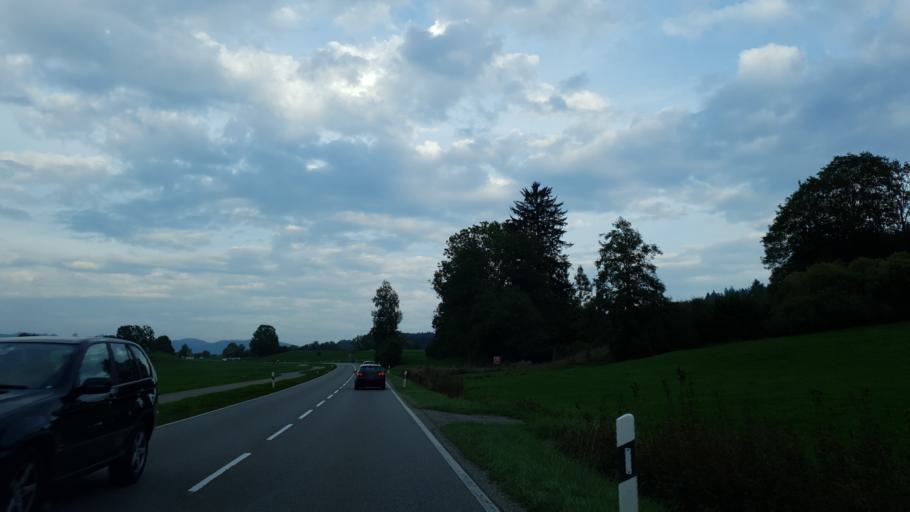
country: DE
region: Baden-Wuerttemberg
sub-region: Tuebingen Region
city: Isny im Allgau
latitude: 47.6837
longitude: 10.0052
